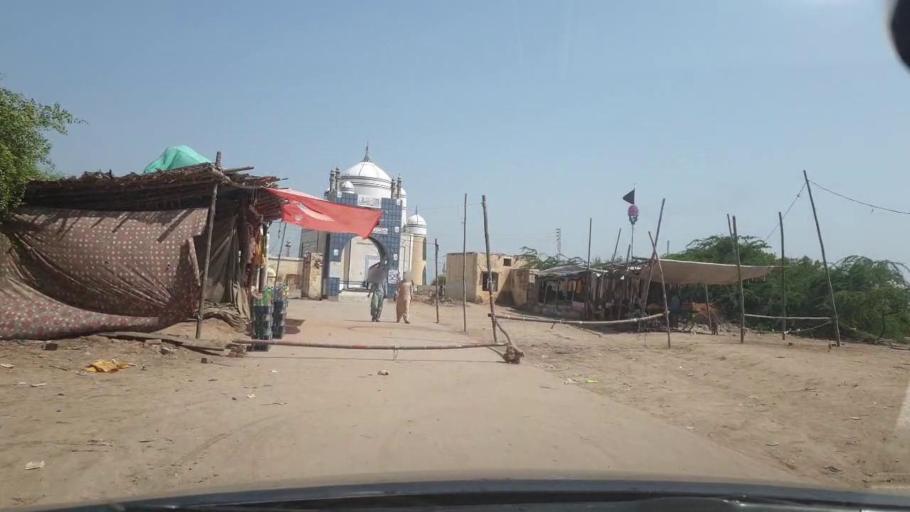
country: PK
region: Sindh
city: Naukot
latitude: 24.8116
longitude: 69.2221
